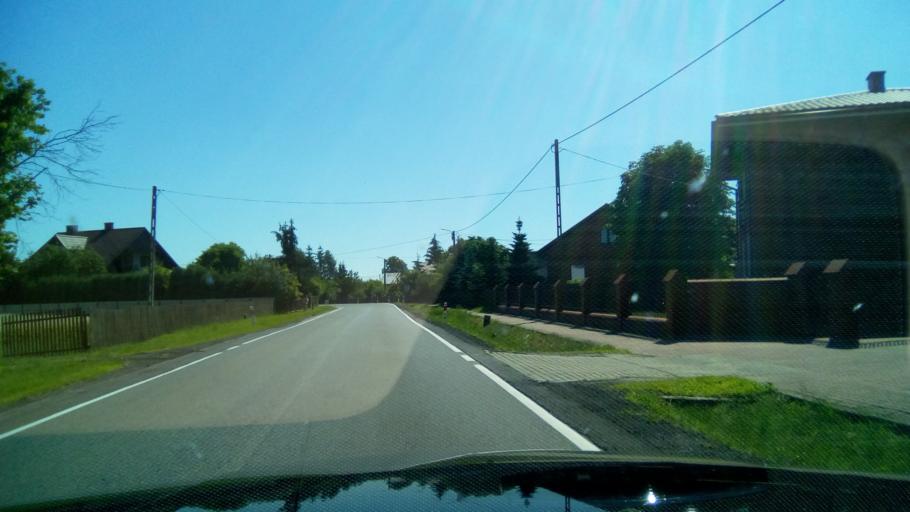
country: PL
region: Lodz Voivodeship
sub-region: Powiat opoczynski
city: Poswietne
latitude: 51.5246
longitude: 20.3460
